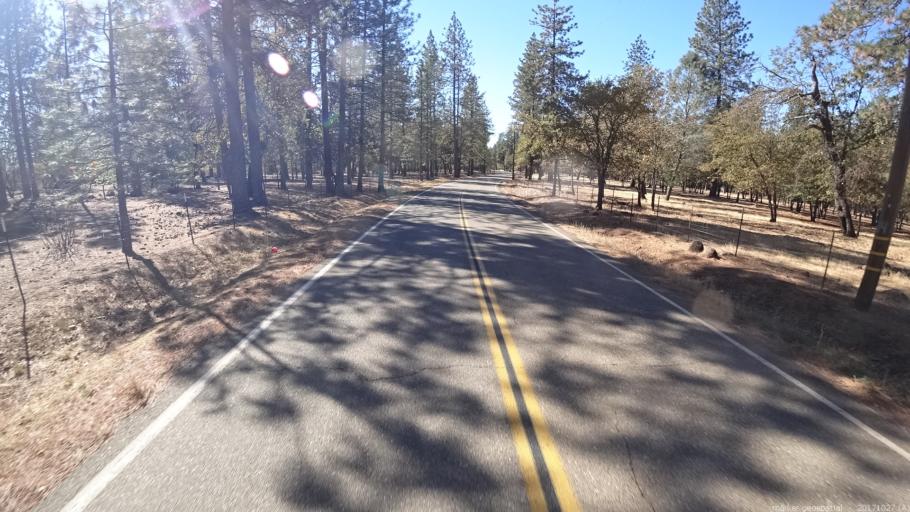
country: US
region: California
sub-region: Shasta County
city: Bella Vista
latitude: 40.6925
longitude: -122.0120
